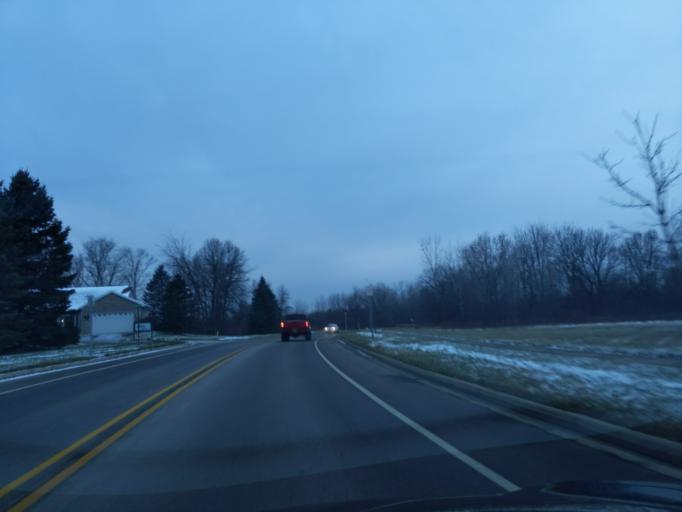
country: US
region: Michigan
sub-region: Ingham County
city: Mason
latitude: 42.5697
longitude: -84.4469
